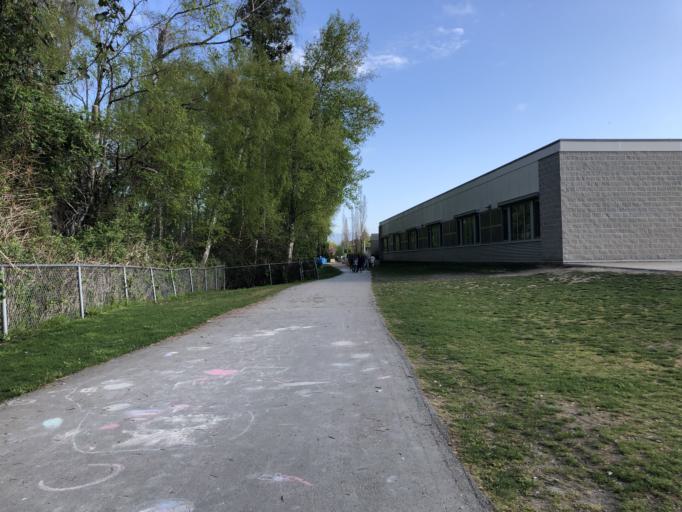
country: CA
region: British Columbia
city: Richmond
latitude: 49.1639
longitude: -123.1197
